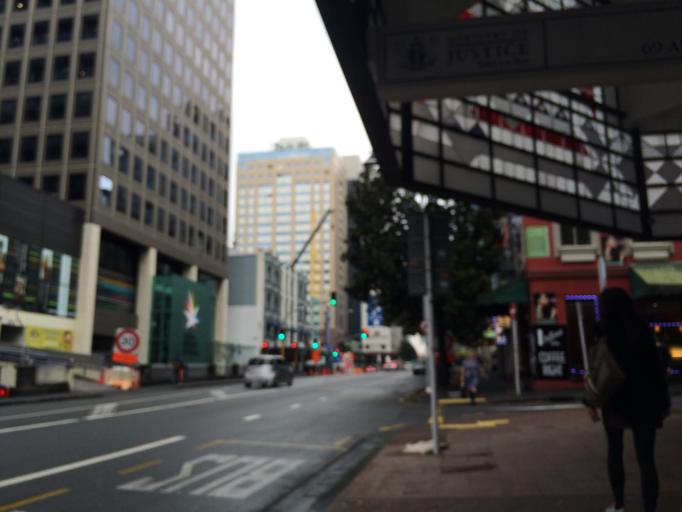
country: NZ
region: Auckland
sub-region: Auckland
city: Auckland
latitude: -36.8476
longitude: 174.7641
